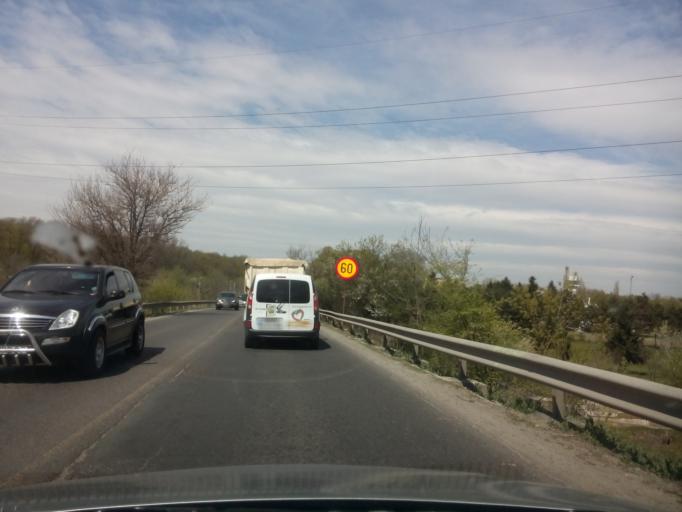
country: RO
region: Ilfov
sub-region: Comuna Pantelimon
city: Pantelimon
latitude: 44.4747
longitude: 26.2300
